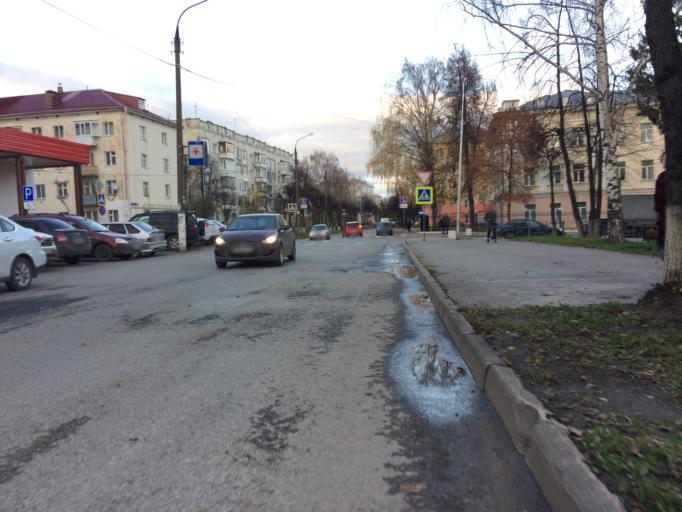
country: RU
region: Mariy-El
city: Yoshkar-Ola
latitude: 56.6279
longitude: 47.8903
